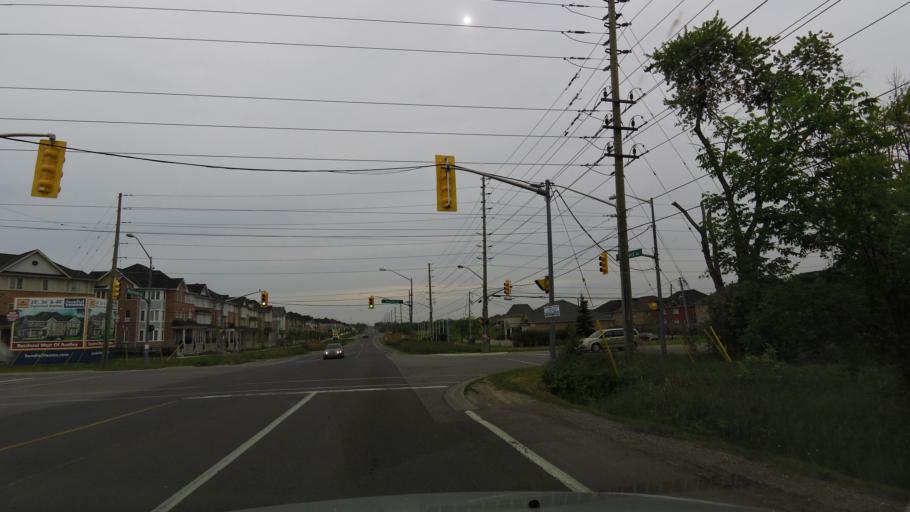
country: CA
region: Ontario
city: Ajax
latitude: 43.8853
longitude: -79.0032
